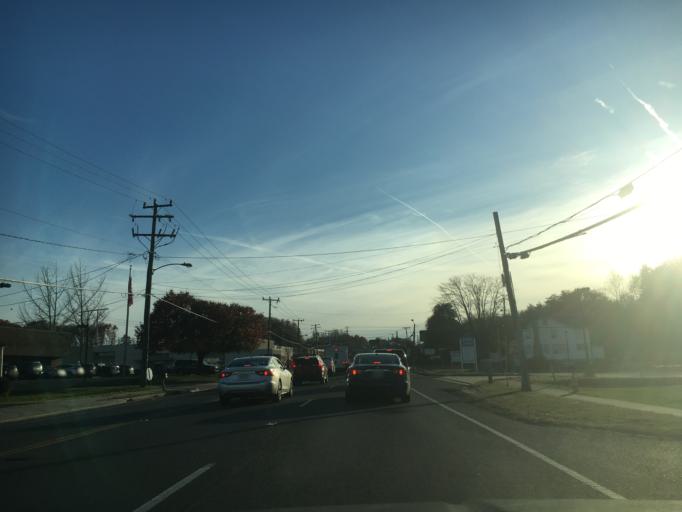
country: US
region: Virginia
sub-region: Prince William County
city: Dumfries
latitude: 38.5635
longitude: -77.3303
